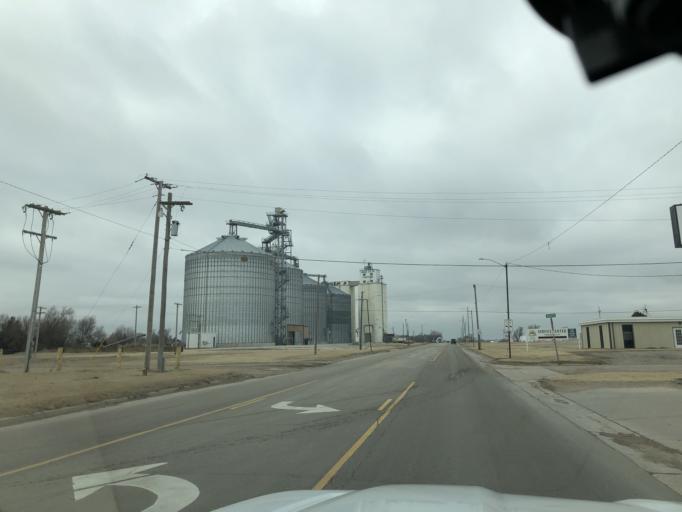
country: US
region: Kansas
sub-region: Stafford County
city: Stafford
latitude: 37.9548
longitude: -98.5957
